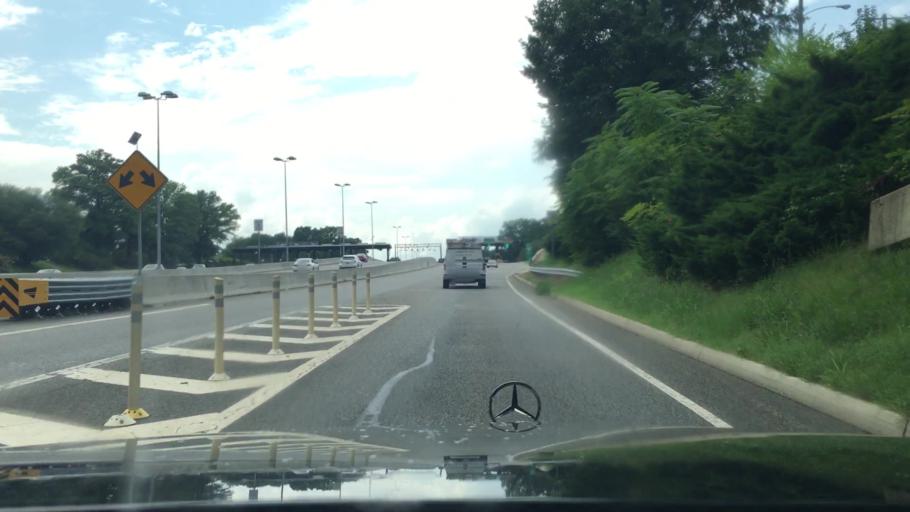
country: US
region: Virginia
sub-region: City of Richmond
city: Richmond
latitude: 37.5444
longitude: -77.4593
